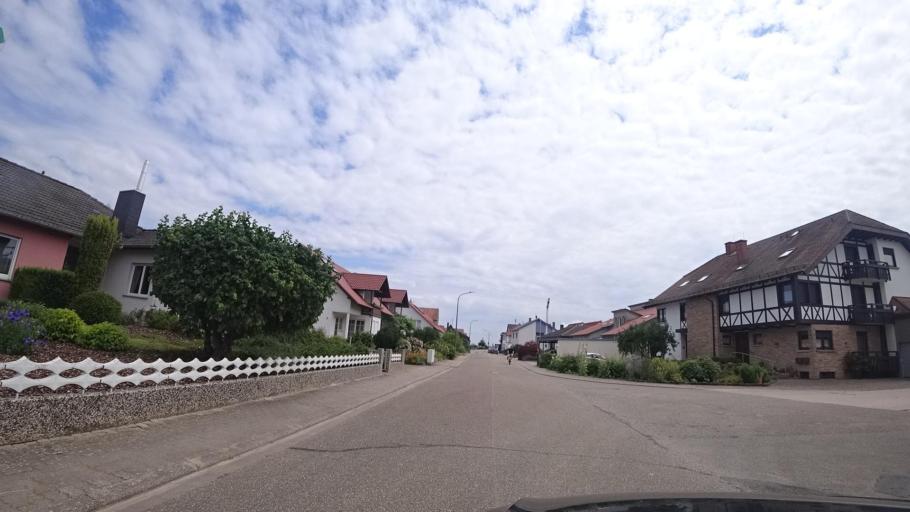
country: DE
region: Rheinland-Pfalz
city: Ottersheim
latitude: 49.1887
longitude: 8.2290
